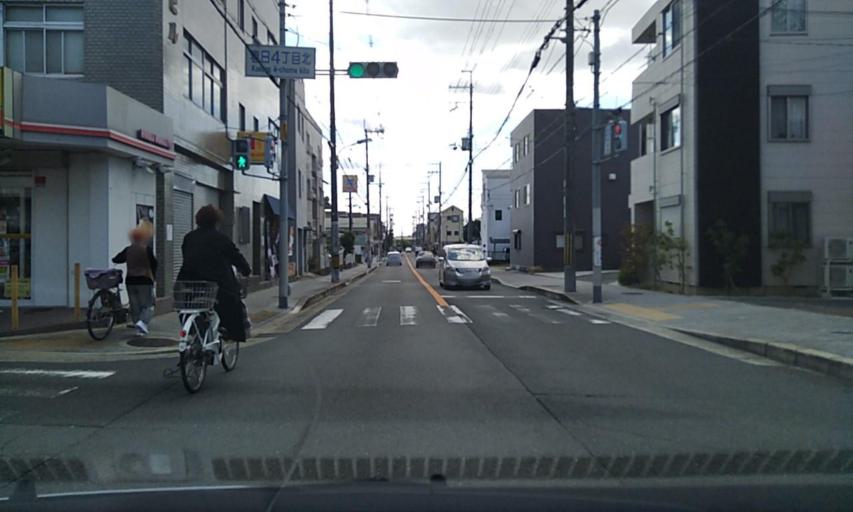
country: JP
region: Osaka
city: Ibaraki
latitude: 34.8240
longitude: 135.5660
